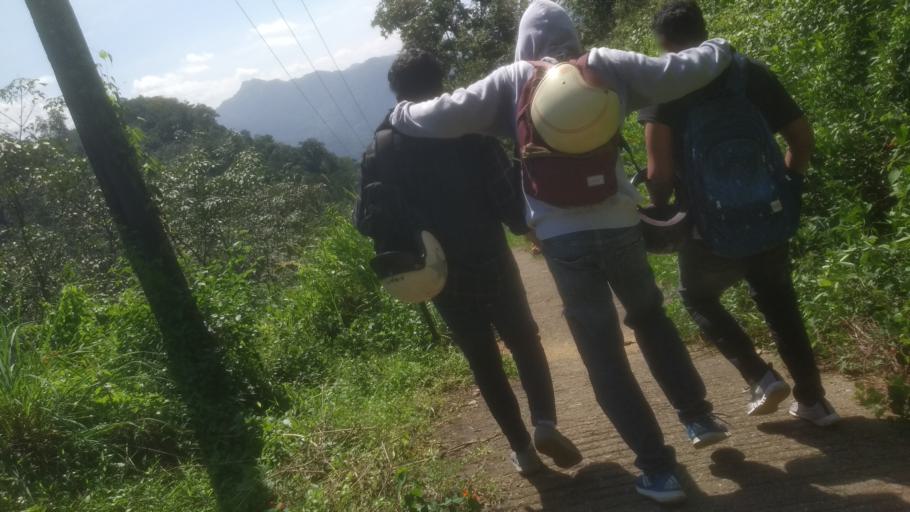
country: IN
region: Kerala
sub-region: Idukki
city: Idukki
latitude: 9.9748
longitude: 76.8379
